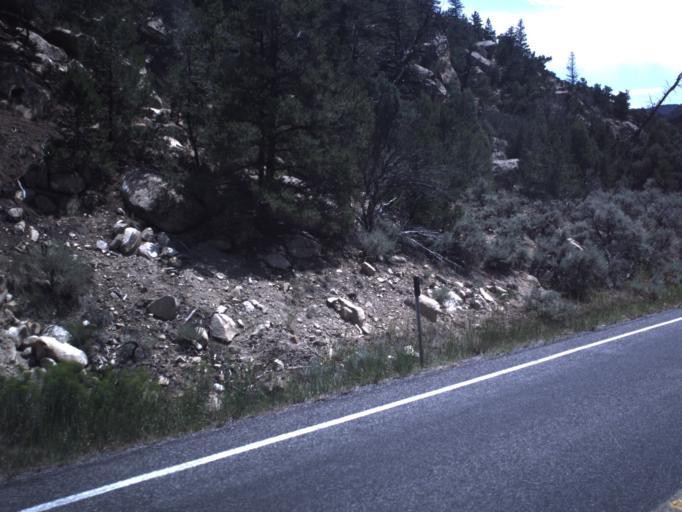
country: US
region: Utah
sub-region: Emery County
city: Huntington
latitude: 39.4210
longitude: -111.1247
